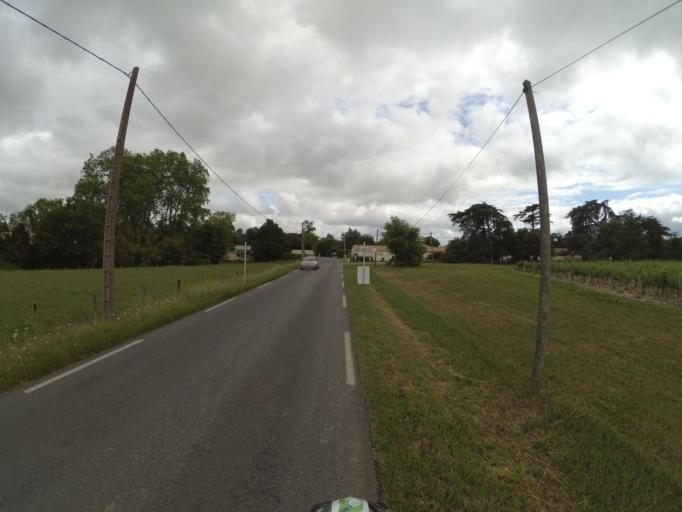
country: FR
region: Aquitaine
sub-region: Departement de la Gironde
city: Macau
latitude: 45.0134
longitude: -0.6193
